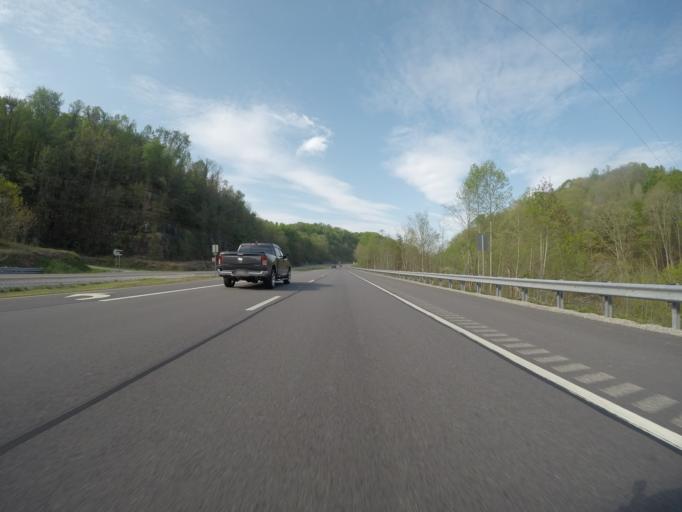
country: US
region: West Virginia
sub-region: Kanawha County
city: Dunbar
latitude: 38.3033
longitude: -81.7373
